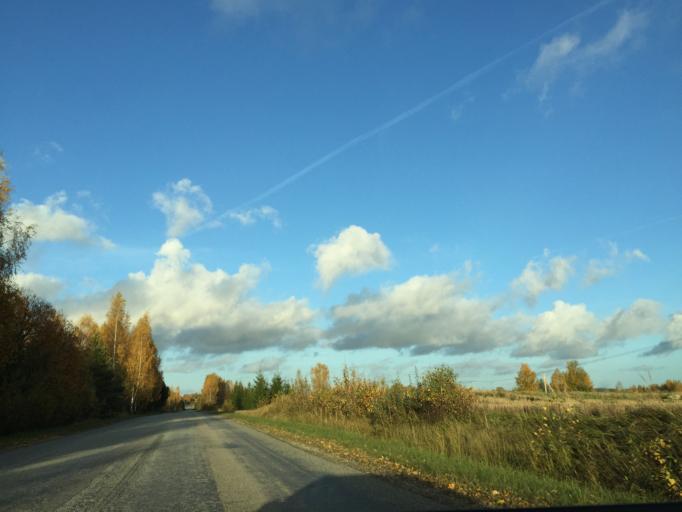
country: LV
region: Ogre
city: Jumprava
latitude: 56.7908
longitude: 25.0340
